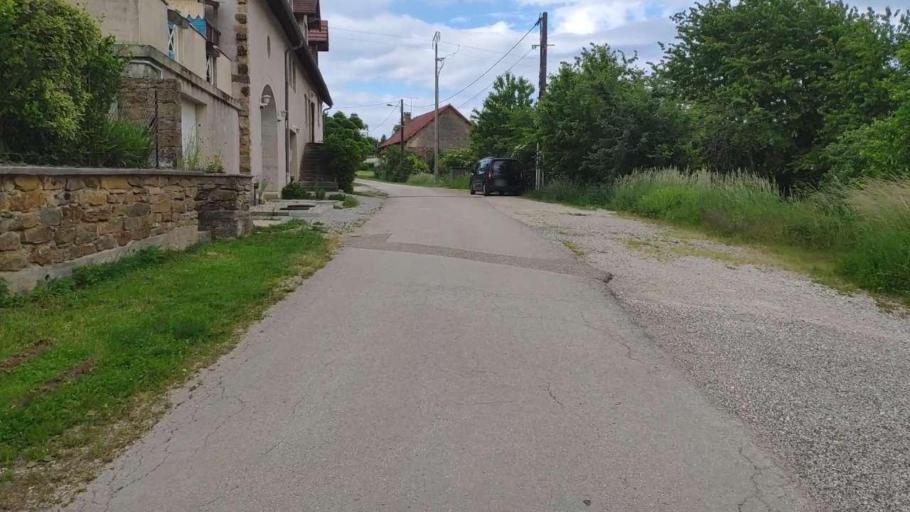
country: FR
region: Franche-Comte
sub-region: Departement du Jura
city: Bletterans
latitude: 46.7930
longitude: 5.5550
